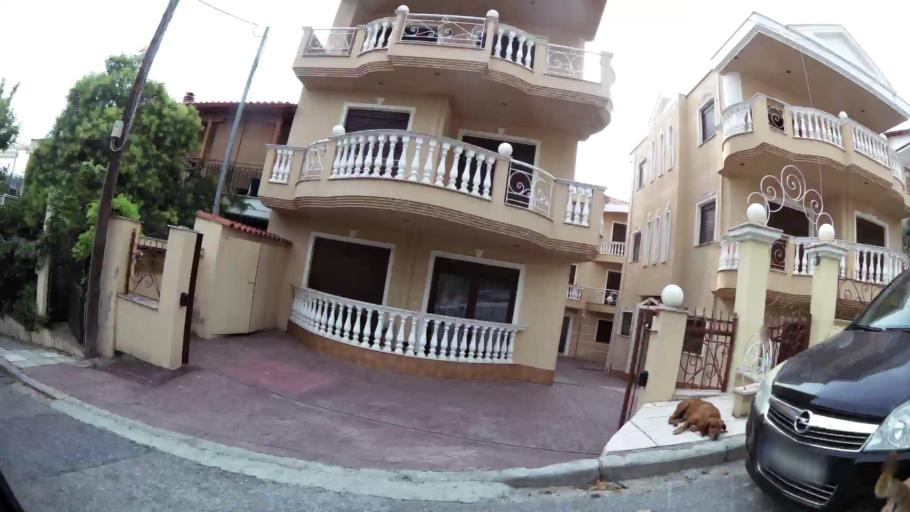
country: GR
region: Central Macedonia
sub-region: Nomos Thessalonikis
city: Oraiokastro
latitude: 40.7325
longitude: 22.9112
